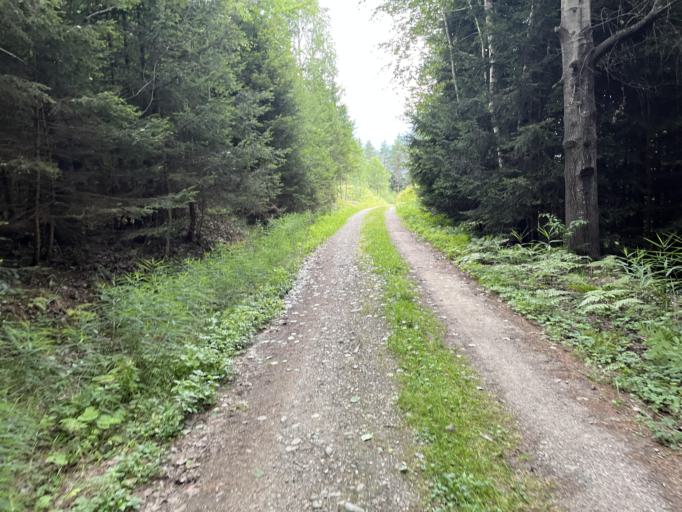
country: AT
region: Carinthia
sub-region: Politischer Bezirk Spittal an der Drau
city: Seeboden
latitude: 46.8019
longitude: 13.5379
